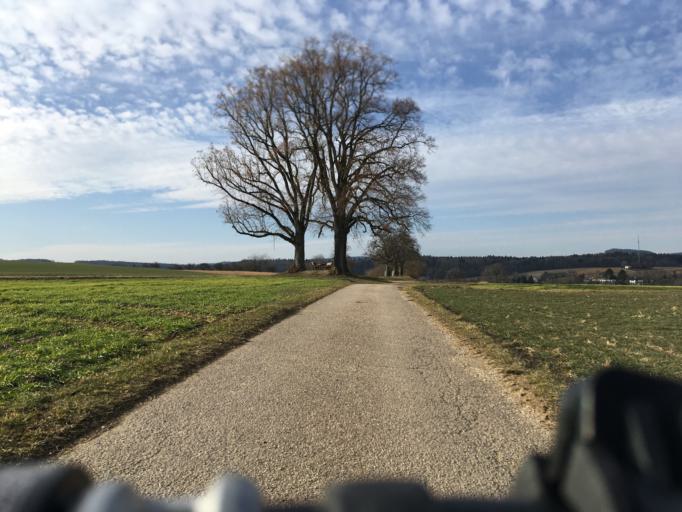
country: CH
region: Schaffhausen
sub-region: Bezirk Reiat
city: Thayngen
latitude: 47.7890
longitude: 8.6935
